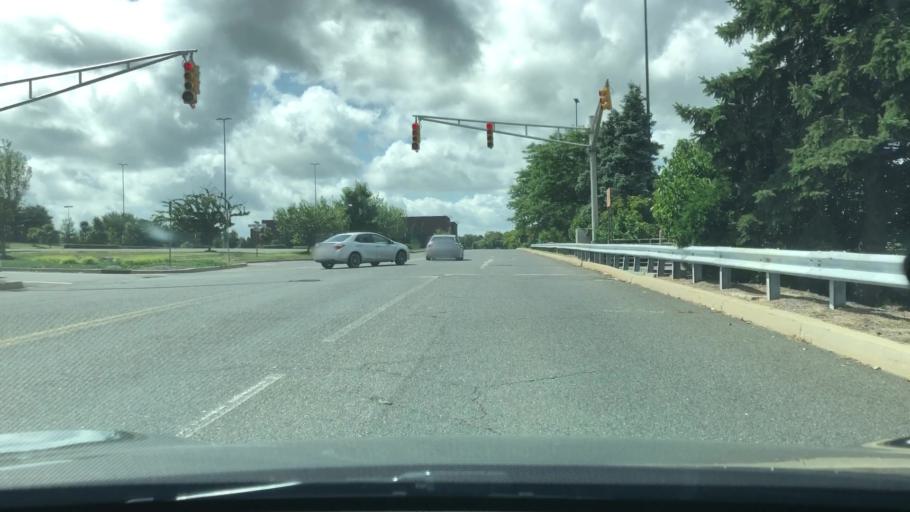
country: US
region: New Jersey
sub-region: Monmouth County
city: West Freehold
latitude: 40.2549
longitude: -74.2971
